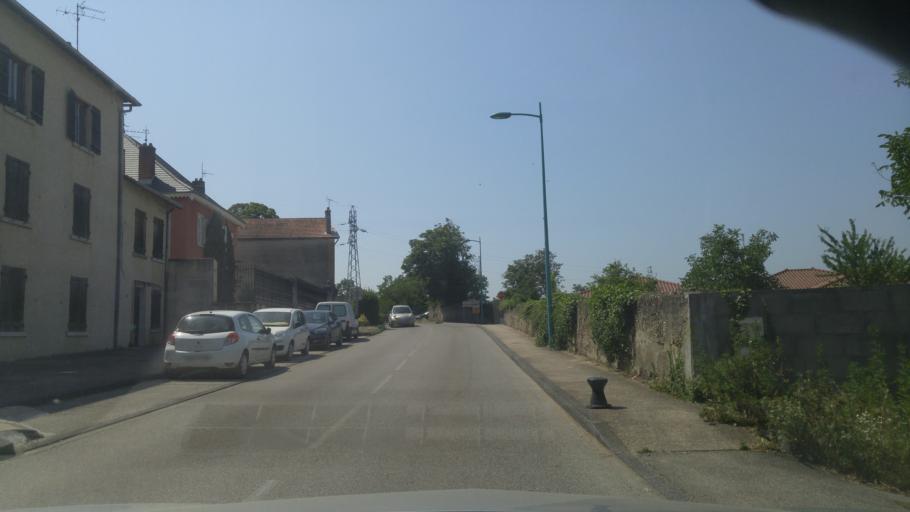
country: FR
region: Rhone-Alpes
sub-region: Departement de l'Isere
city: Pont-de-Cheruy
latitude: 45.7475
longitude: 5.1760
